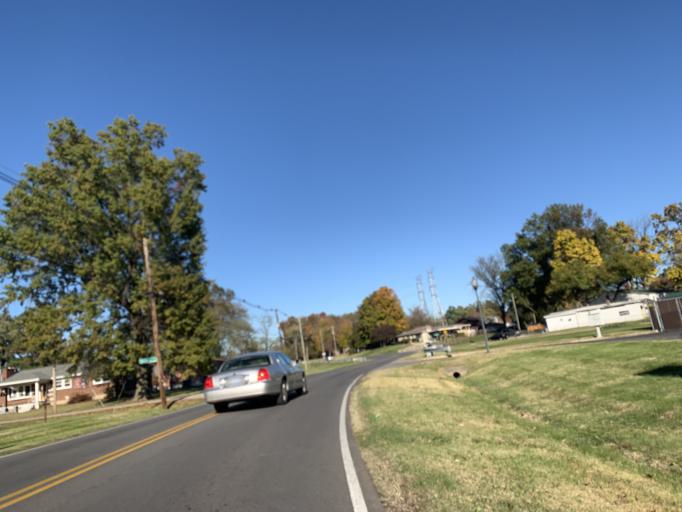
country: US
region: Kentucky
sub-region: Jefferson County
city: Pleasure Ridge Park
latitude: 38.1644
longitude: -85.8438
